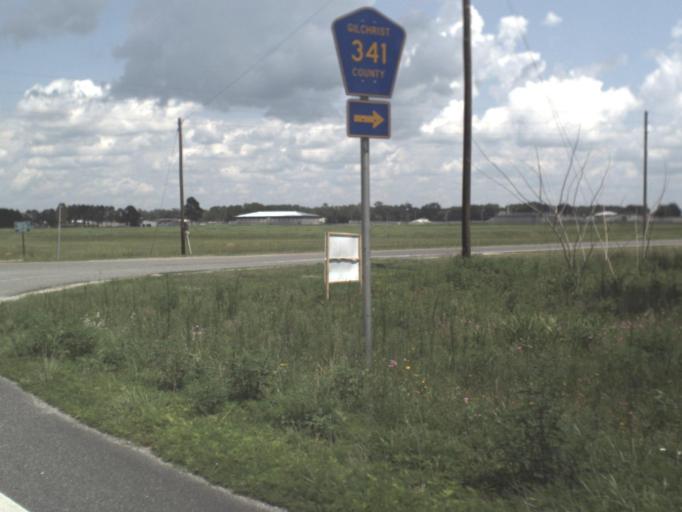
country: US
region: Florida
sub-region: Gilchrist County
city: Trenton
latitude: 29.6127
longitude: -82.8738
